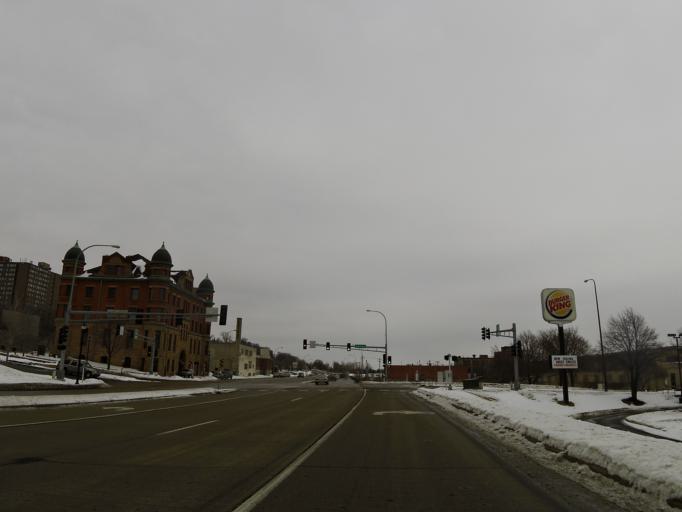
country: US
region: Minnesota
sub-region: Dakota County
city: South Saint Paul
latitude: 44.8927
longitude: -93.0339
